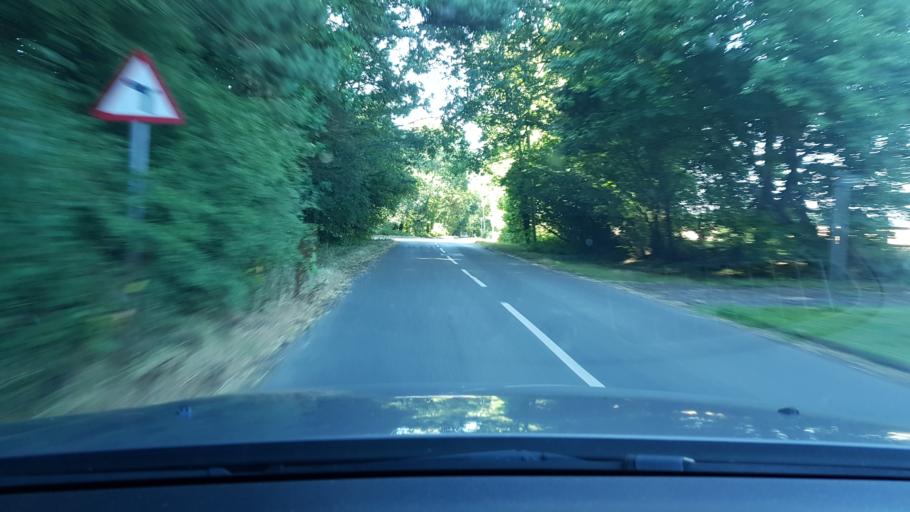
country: GB
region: England
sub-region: Wiltshire
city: Chilton Foliat
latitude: 51.4684
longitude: -1.5507
